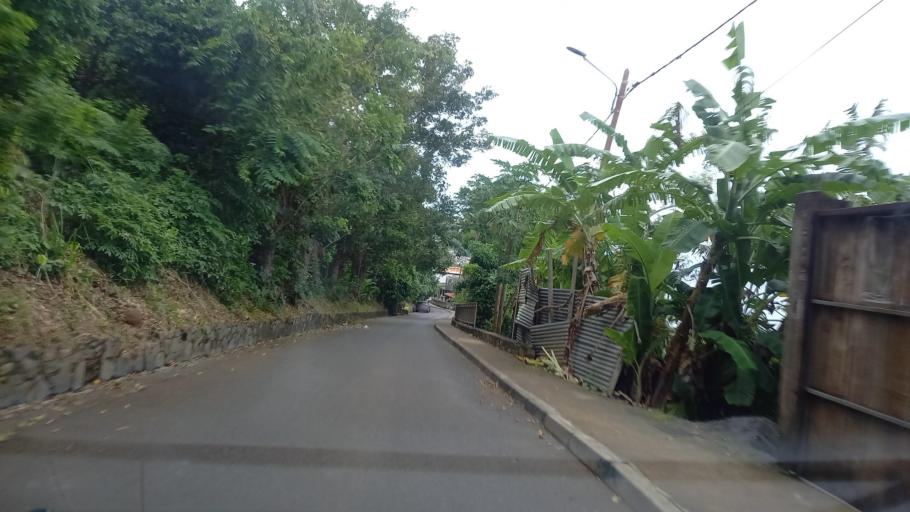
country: YT
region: Sada
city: Sada
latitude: -12.8457
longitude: 45.1022
